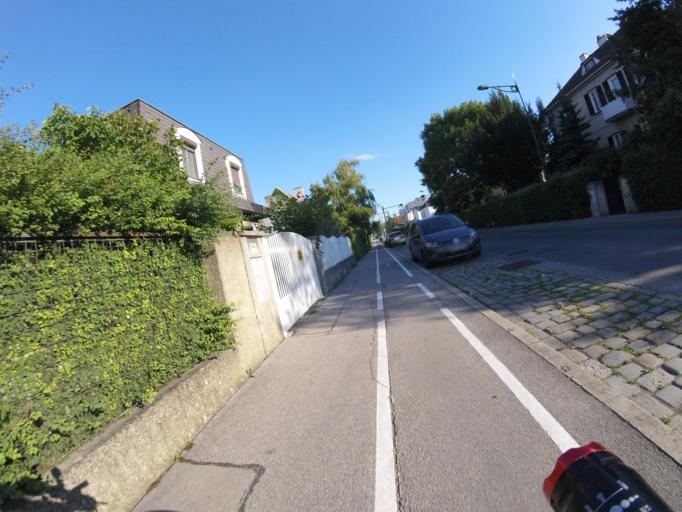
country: AT
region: Lower Austria
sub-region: Politischer Bezirk Modling
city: Modling
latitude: 48.0794
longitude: 16.2958
